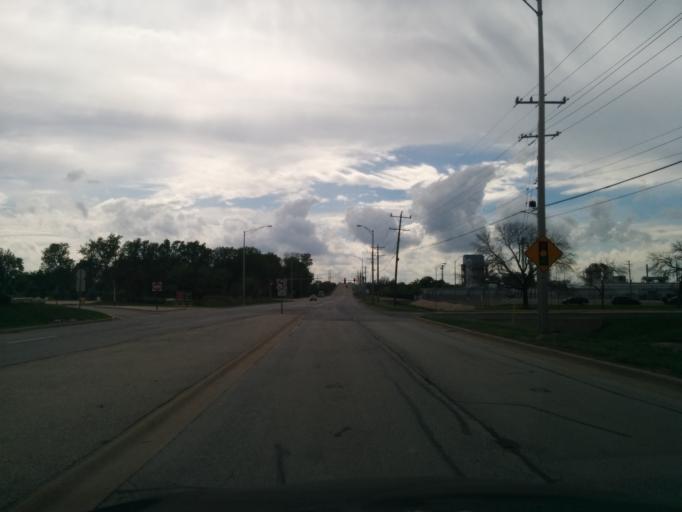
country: US
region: Illinois
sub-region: Will County
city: Romeoville
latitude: 41.6409
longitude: -88.0507
